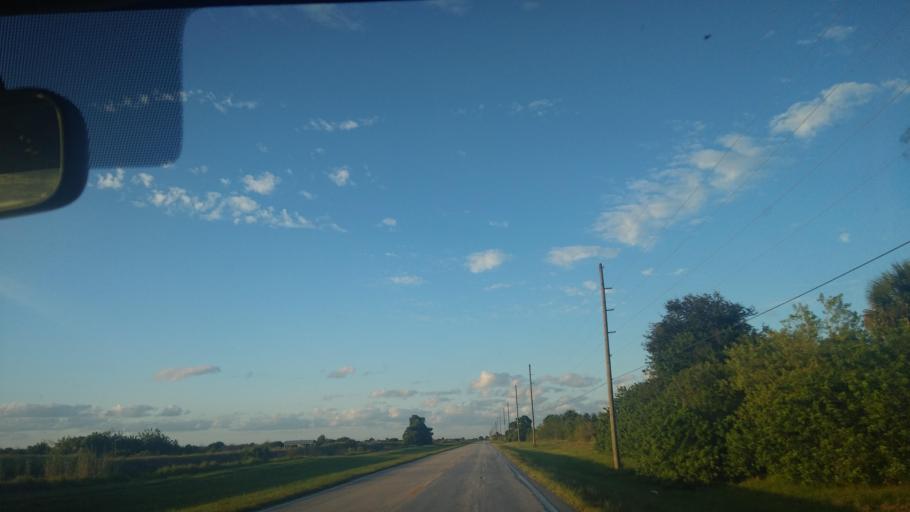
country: US
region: Florida
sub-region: Indian River County
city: Fellsmere
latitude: 27.7272
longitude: -80.6424
